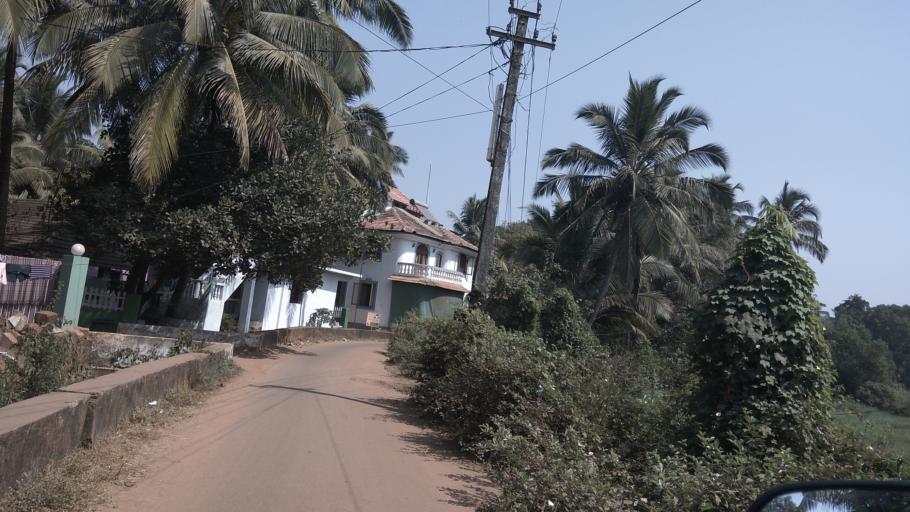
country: IN
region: Goa
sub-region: North Goa
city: Candolim
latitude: 15.5221
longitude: 73.7705
